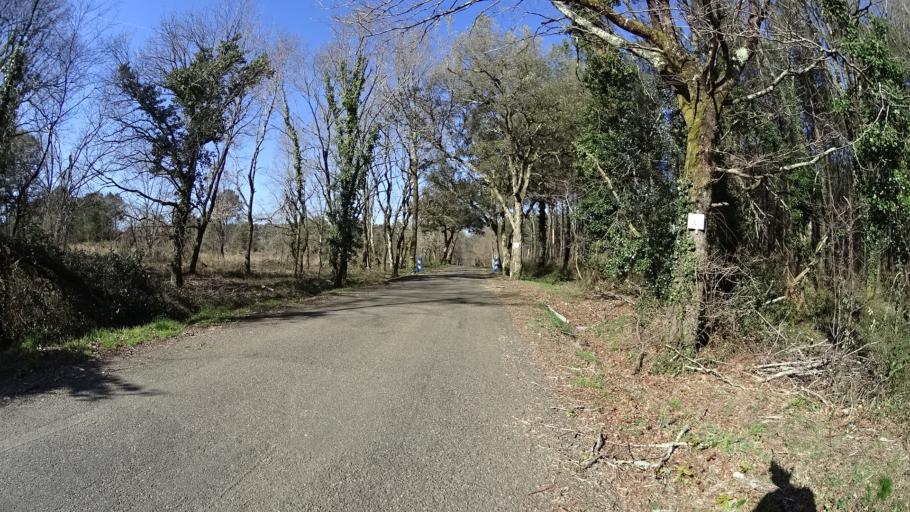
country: FR
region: Aquitaine
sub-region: Departement des Landes
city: Mees
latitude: 43.7424
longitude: -1.0969
